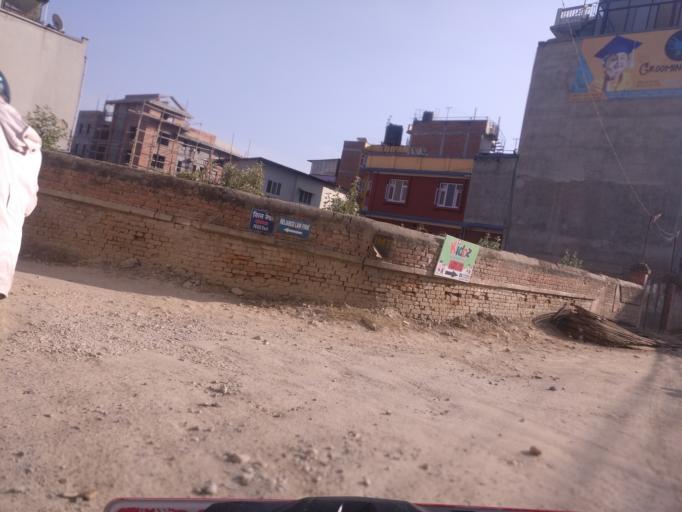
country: NP
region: Central Region
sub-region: Bagmati Zone
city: Patan
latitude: 27.6733
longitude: 85.3157
